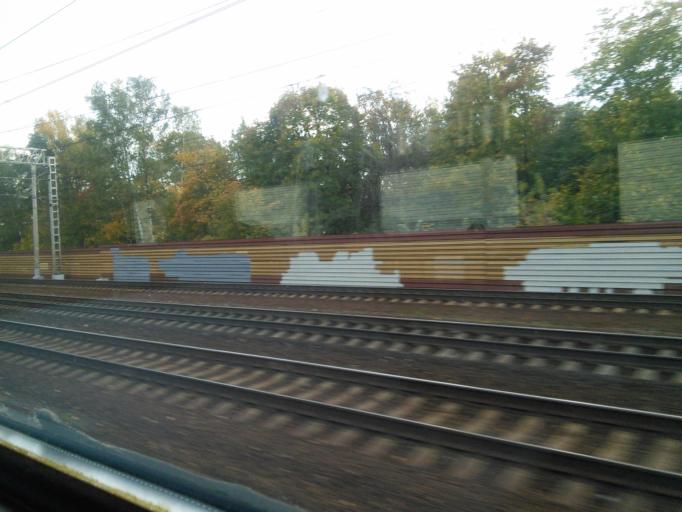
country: RU
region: Moskovskaya
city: Levoberezhnaya
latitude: 55.8858
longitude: 37.4713
